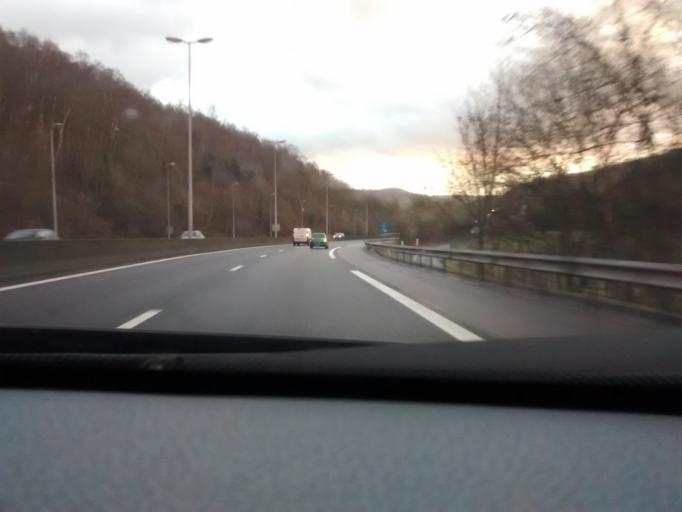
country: FR
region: Haute-Normandie
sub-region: Departement de la Seine-Maritime
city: Darnetal
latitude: 49.4598
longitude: 1.1430
